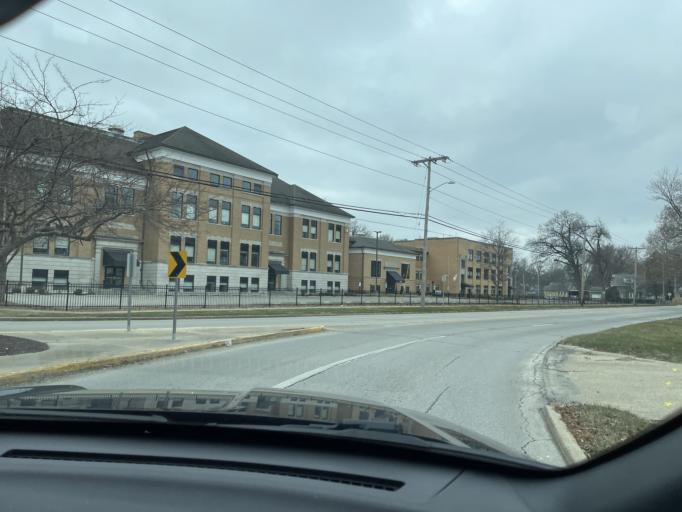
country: US
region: Illinois
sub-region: Sangamon County
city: Springfield
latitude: 39.7944
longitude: -89.6587
